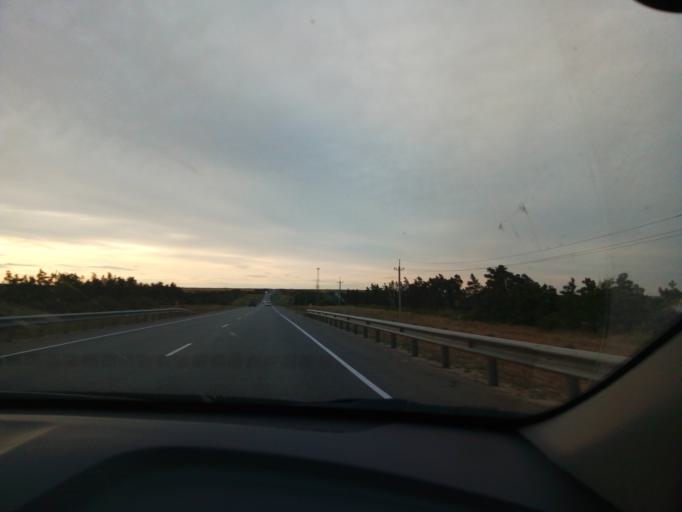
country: RU
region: Volgograd
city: Primorsk
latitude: 49.2573
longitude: 44.8848
